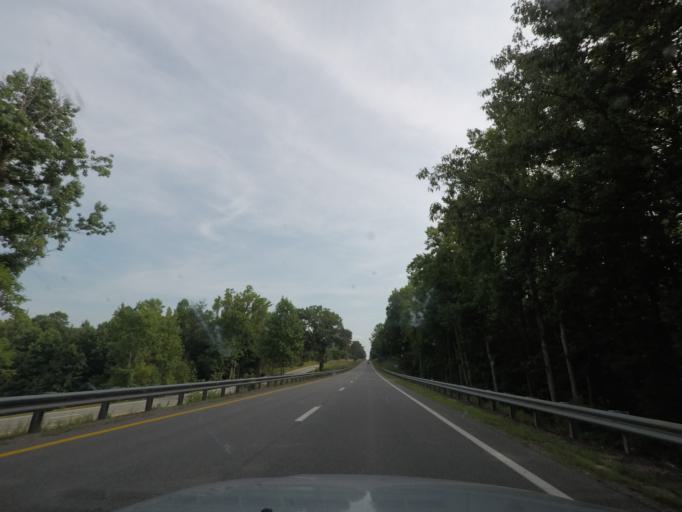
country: US
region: Virginia
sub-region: Charlotte County
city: Charlotte Court House
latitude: 36.9792
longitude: -78.4890
